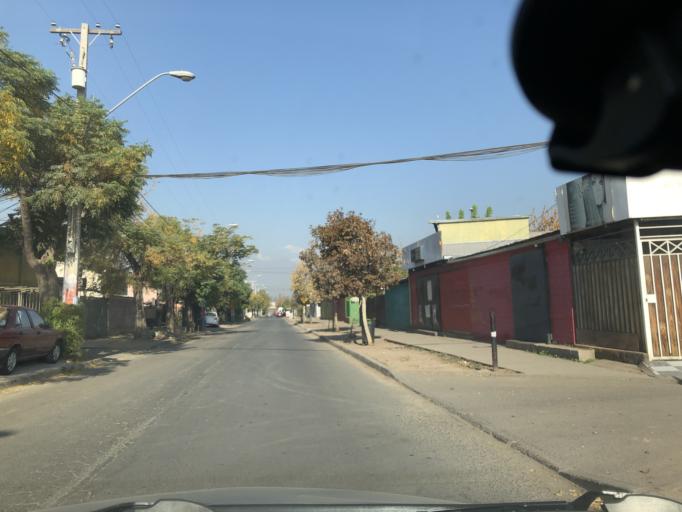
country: CL
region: Santiago Metropolitan
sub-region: Provincia de Cordillera
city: Puente Alto
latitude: -33.6107
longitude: -70.5530
